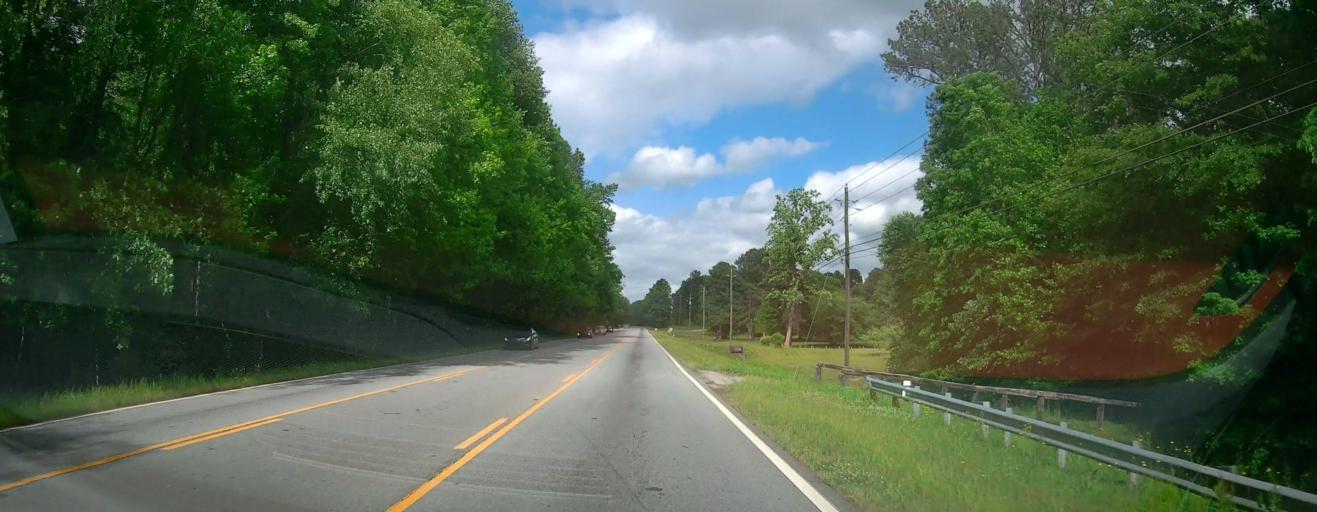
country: US
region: Georgia
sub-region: Rockdale County
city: Conyers
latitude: 33.6971
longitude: -83.9561
